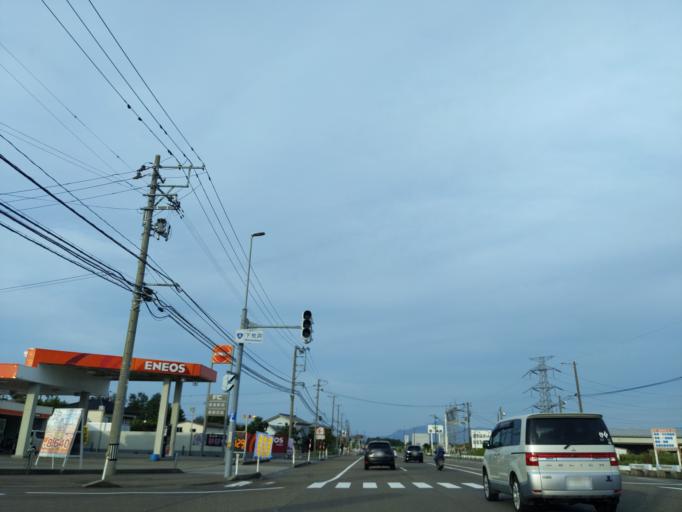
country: JP
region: Niigata
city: Joetsu
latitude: 37.1935
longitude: 138.2814
